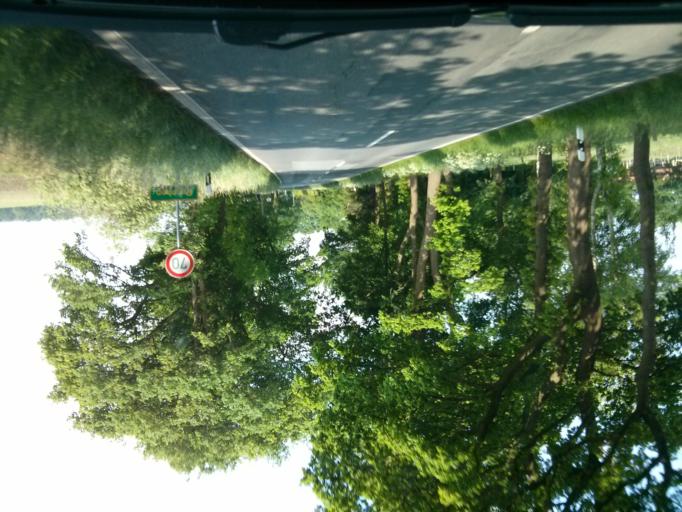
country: DE
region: Lower Saxony
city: Schiffdorf
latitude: 53.5155
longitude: 8.6884
